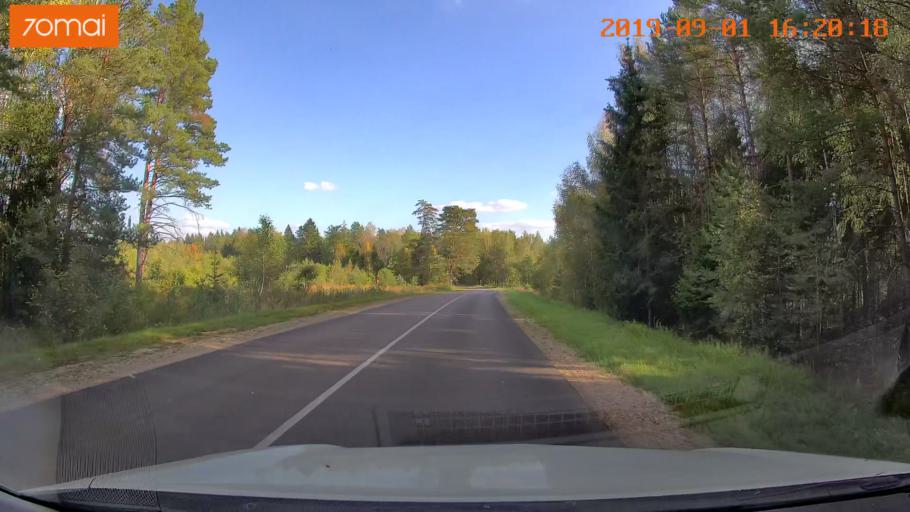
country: RU
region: Kaluga
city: Maloyaroslavets
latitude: 54.8805
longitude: 36.5336
